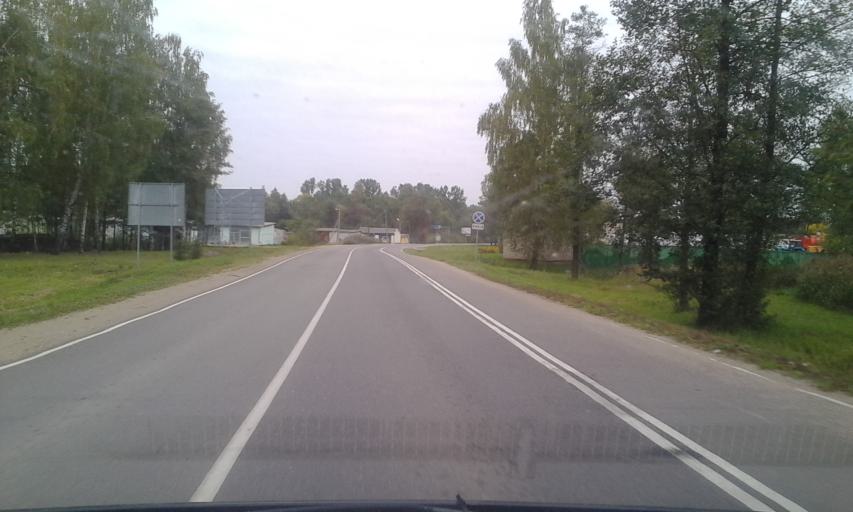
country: BY
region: Vitebsk
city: Pastavy
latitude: 55.1152
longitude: 26.8720
